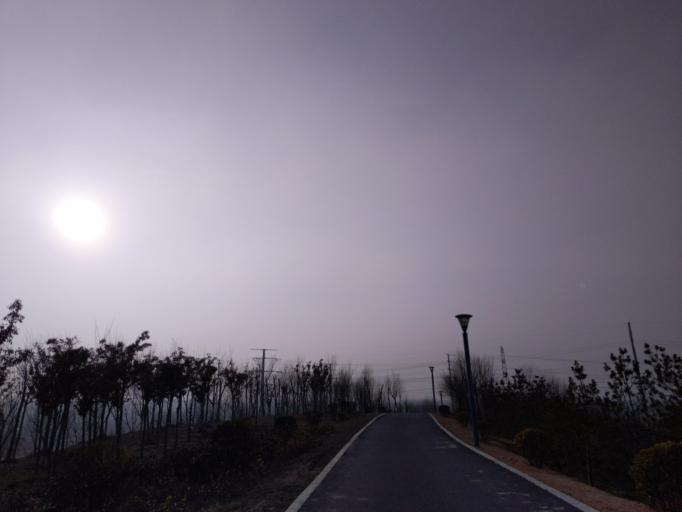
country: CN
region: Henan Sheng
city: Puyang
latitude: 35.8203
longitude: 115.0017
